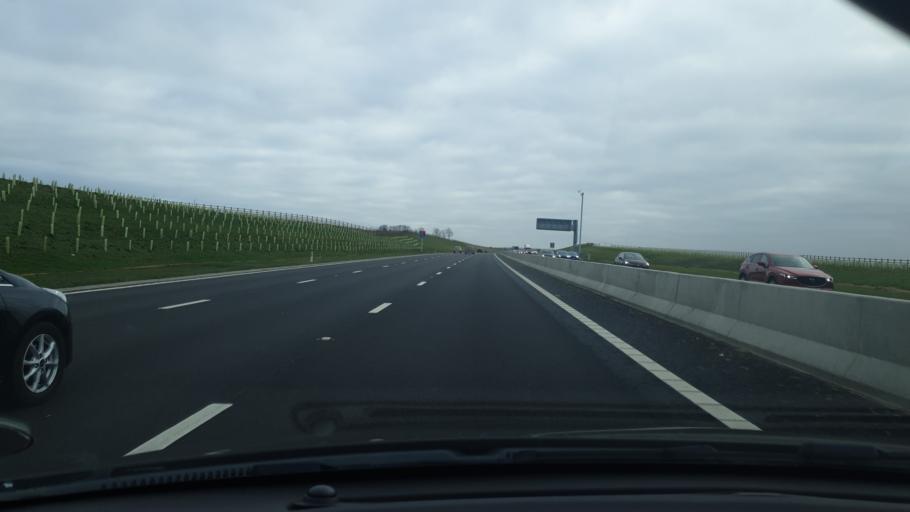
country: GB
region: England
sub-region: Cambridgeshire
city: Brampton
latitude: 52.2990
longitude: -0.2000
